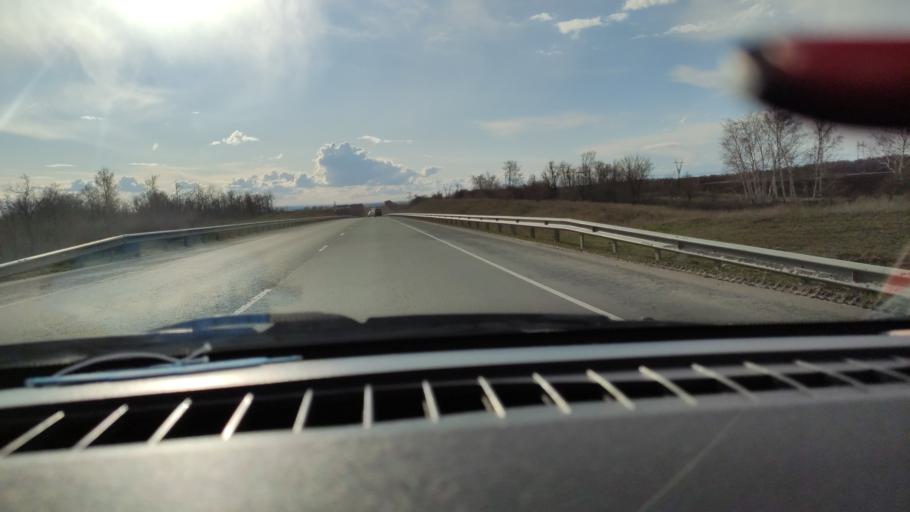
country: RU
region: Saratov
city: Yelshanka
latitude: 51.8221
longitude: 46.3291
